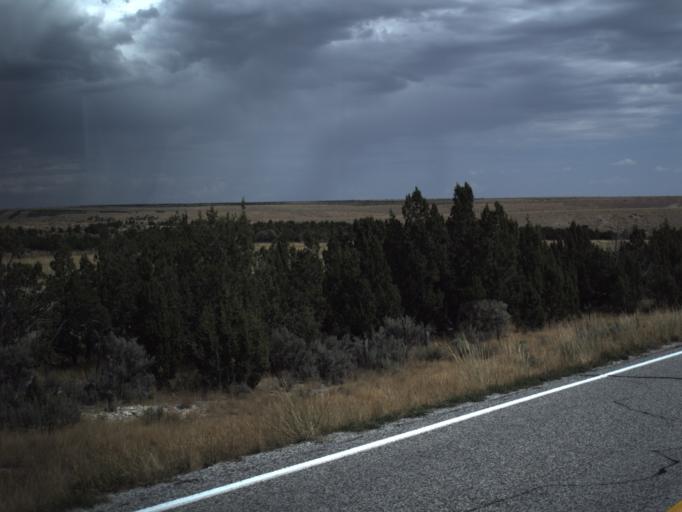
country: US
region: Idaho
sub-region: Cassia County
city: Burley
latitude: 41.8173
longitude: -113.2564
